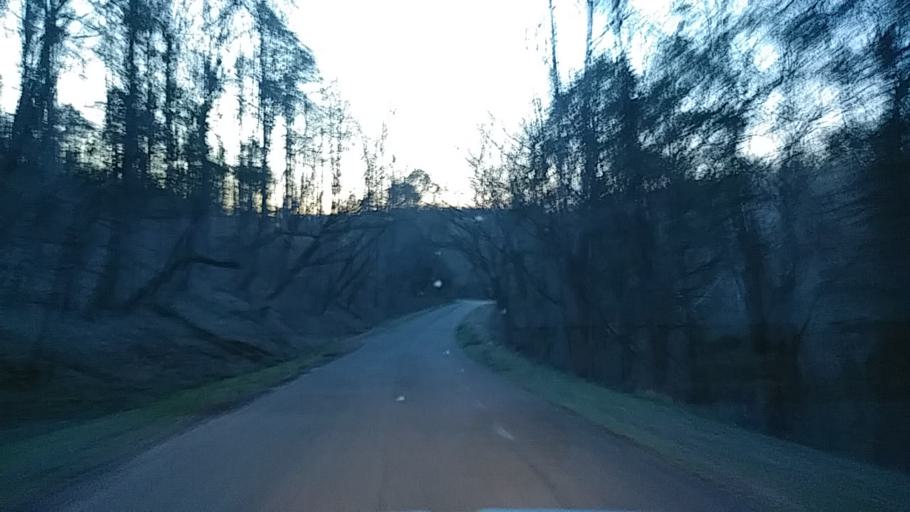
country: US
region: Tennessee
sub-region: Greene County
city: Mosheim
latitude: 36.0609
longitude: -82.9762
